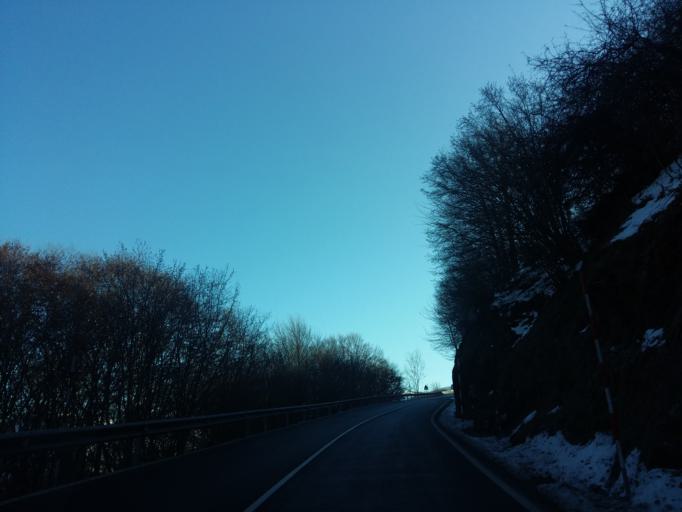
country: ES
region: Basque Country
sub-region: Bizkaia
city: Lanestosa
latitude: 43.1532
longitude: -3.4419
